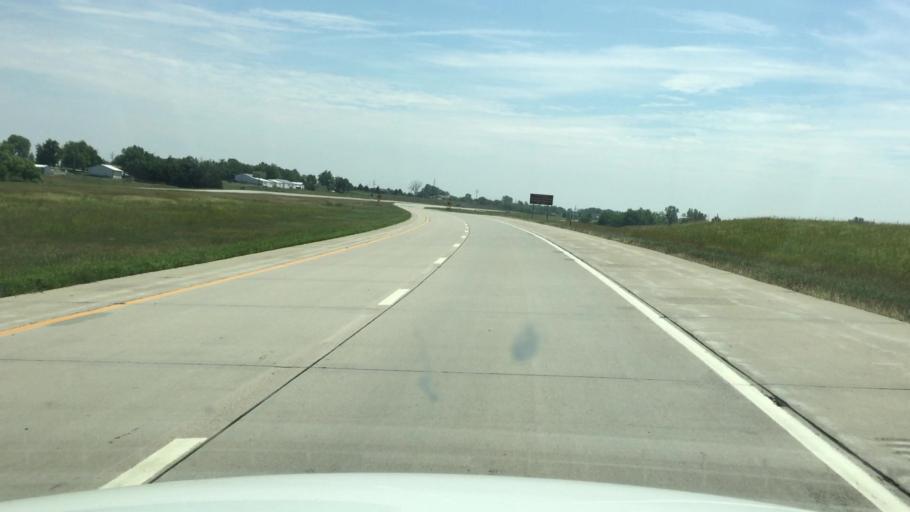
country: US
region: Kansas
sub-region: Jackson County
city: Holton
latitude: 39.3360
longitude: -95.7266
